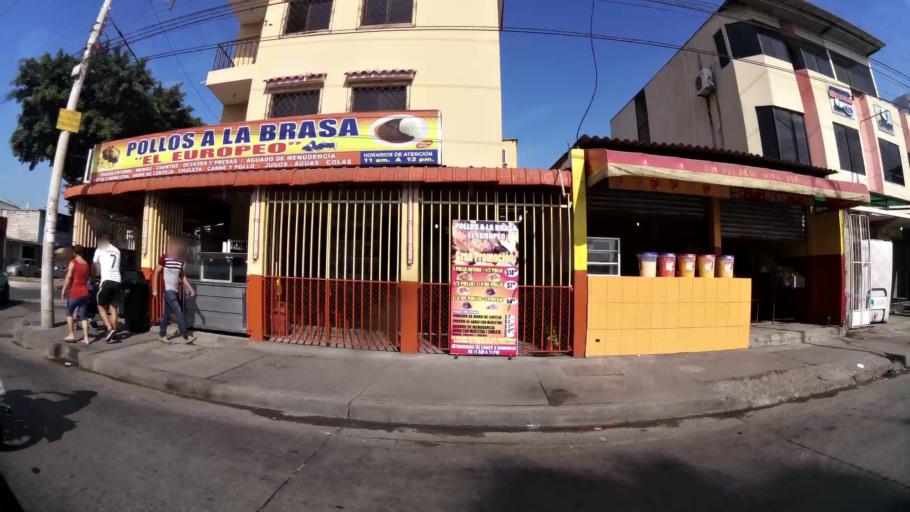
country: EC
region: Guayas
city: Eloy Alfaro
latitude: -2.0850
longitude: -79.9147
